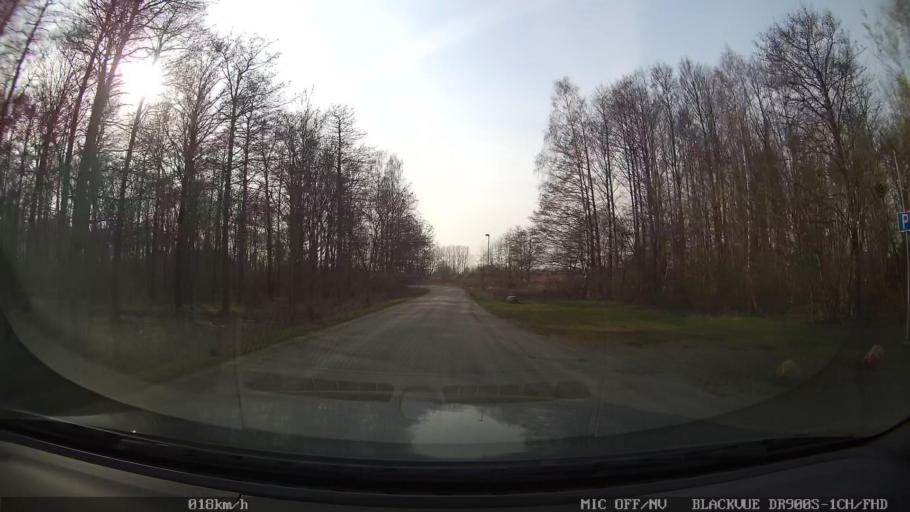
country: SE
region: Skane
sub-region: Ystads Kommun
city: Ystad
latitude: 55.4418
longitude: 13.8534
